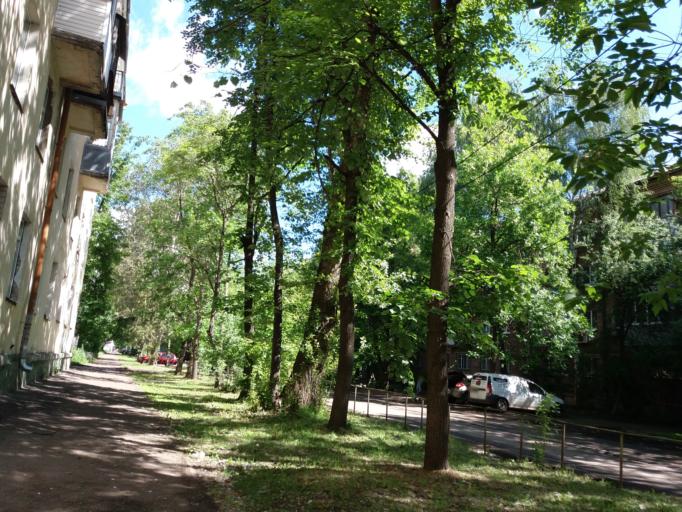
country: RU
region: Jaroslavl
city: Yaroslavl
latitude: 57.6379
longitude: 39.8437
